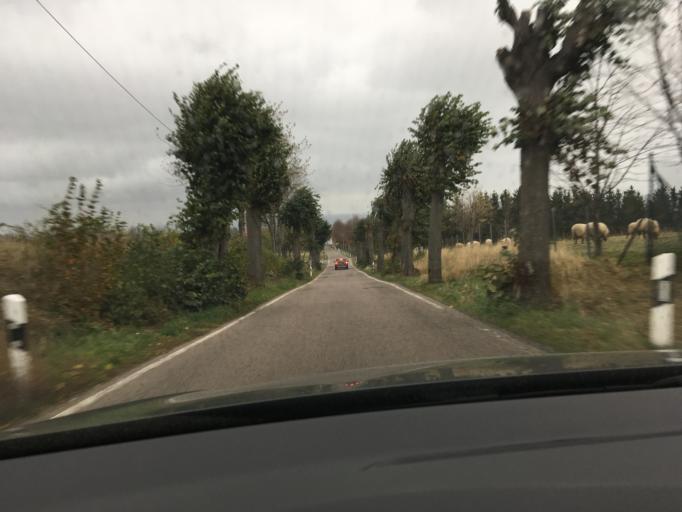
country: DE
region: Saxony
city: Kreischa
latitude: 50.9220
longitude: 13.7974
